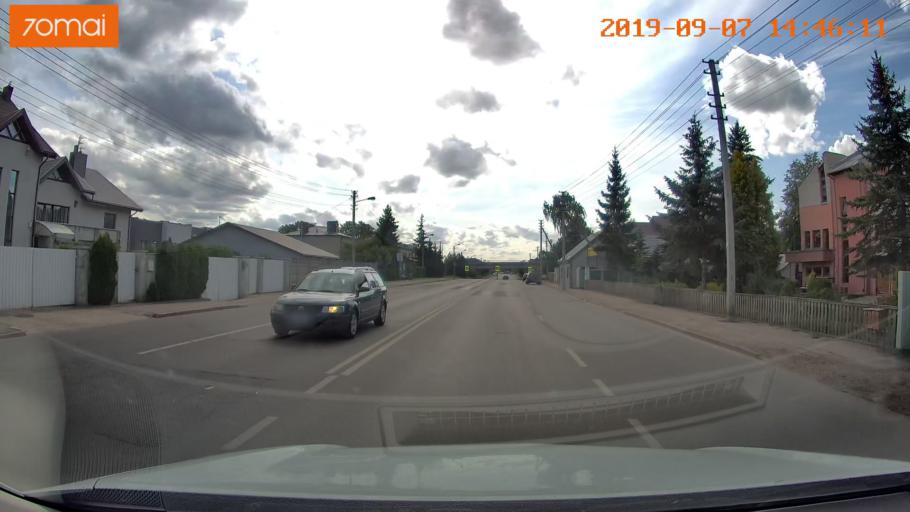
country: LT
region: Kauno apskritis
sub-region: Kaunas
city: Silainiai
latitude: 54.9275
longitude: 23.9057
